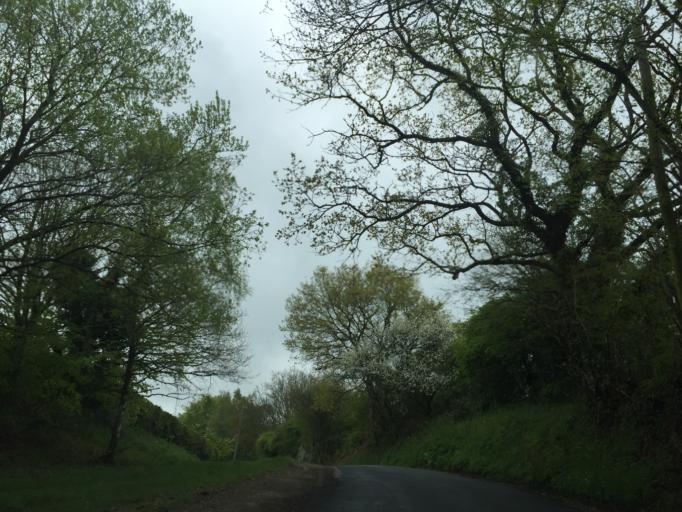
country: GB
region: England
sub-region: East Sussex
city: Heathfield
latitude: 50.9965
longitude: 0.2856
